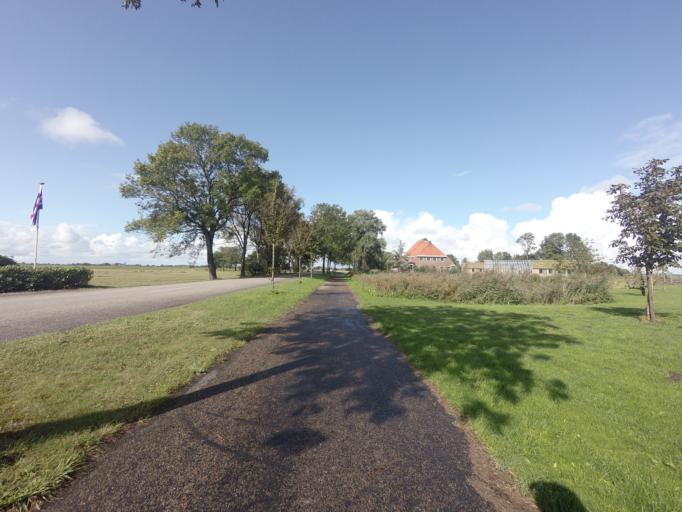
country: NL
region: Friesland
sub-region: Gemeente Boarnsterhim
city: Warten
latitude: 53.1501
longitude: 5.8786
